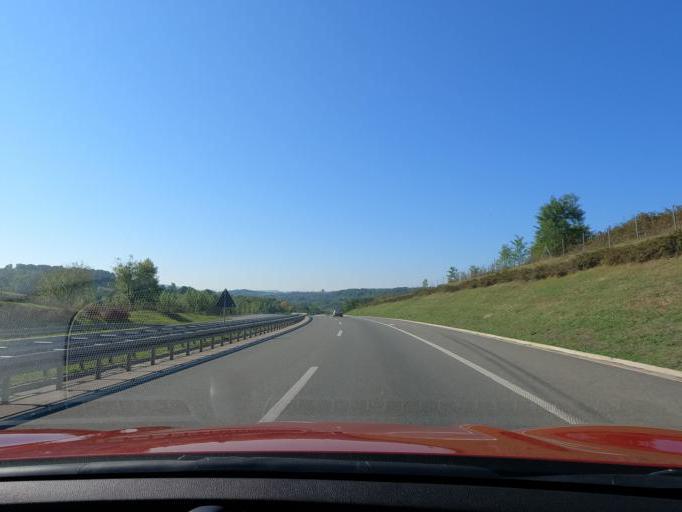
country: RS
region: Central Serbia
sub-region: Moravicki Okrug
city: Gornji Milanovac
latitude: 44.0937
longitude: 20.3791
